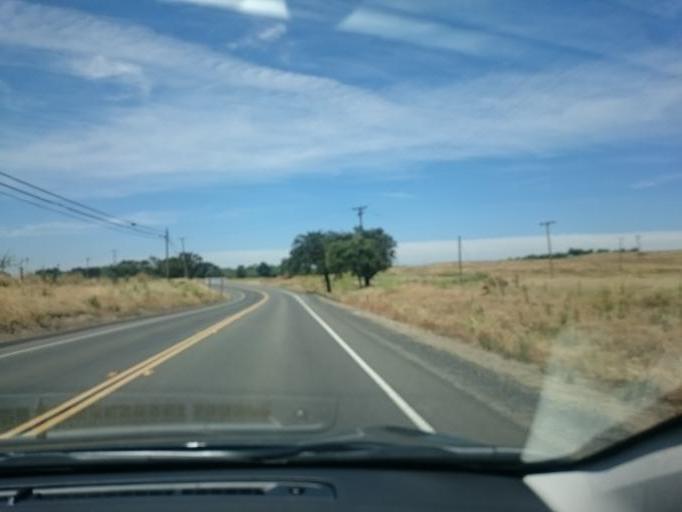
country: US
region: California
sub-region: Stanislaus County
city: Waterford
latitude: 37.6467
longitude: -120.6967
